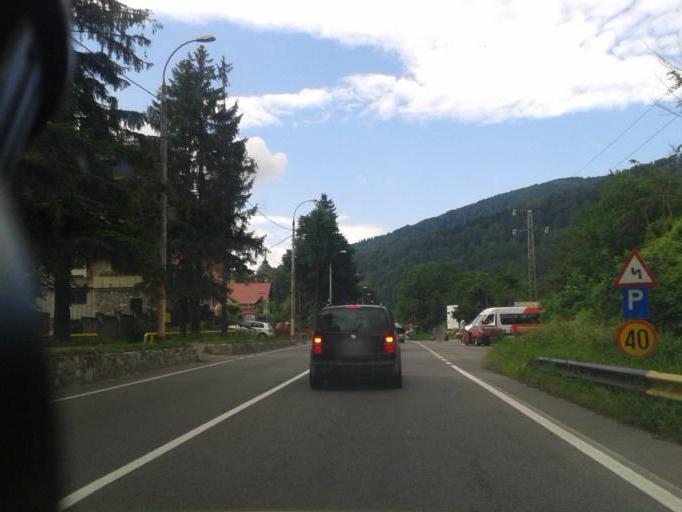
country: RO
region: Prahova
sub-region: Oras Sinaia
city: Sinaia
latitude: 45.3240
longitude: 25.5643
